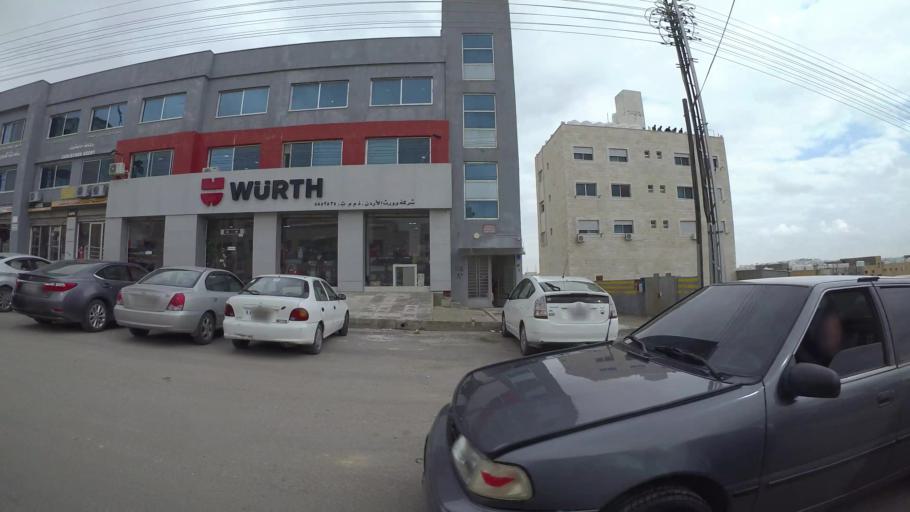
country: JO
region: Amman
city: Wadi as Sir
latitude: 31.9420
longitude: 35.8324
